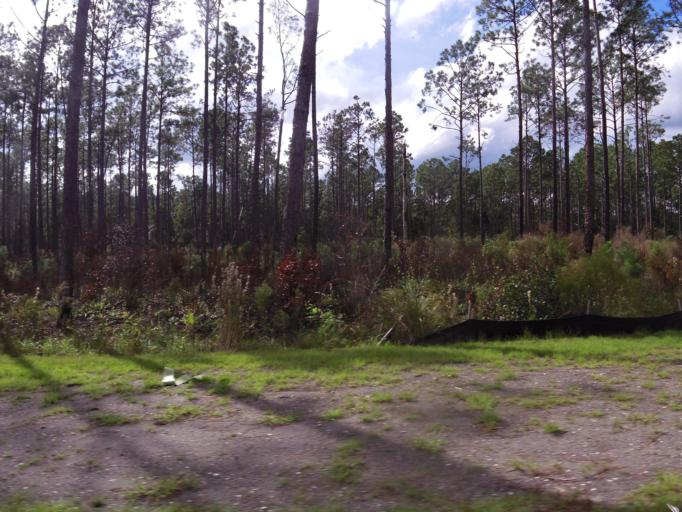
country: US
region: Florida
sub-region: Saint Johns County
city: Villano Beach
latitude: 29.9961
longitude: -81.3935
